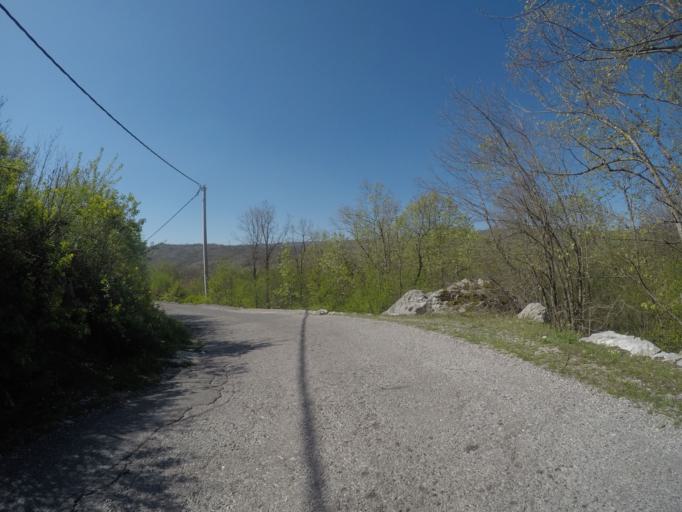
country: ME
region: Danilovgrad
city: Danilovgrad
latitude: 42.5250
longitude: 19.0471
